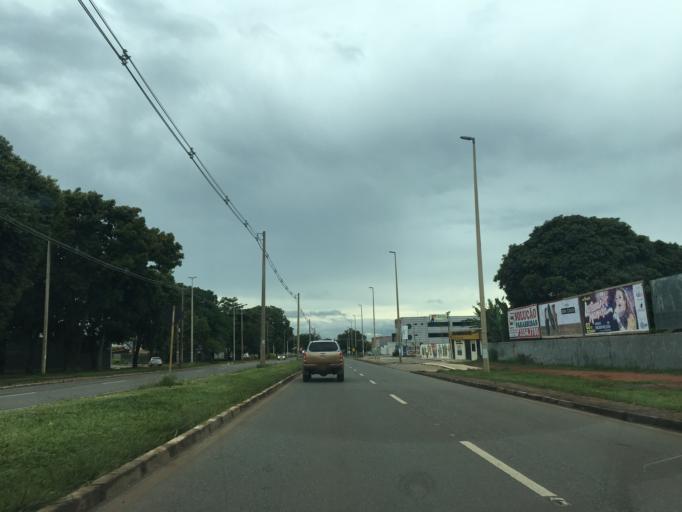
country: BR
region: Goias
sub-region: Luziania
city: Luziania
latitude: -16.0202
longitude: -48.0605
